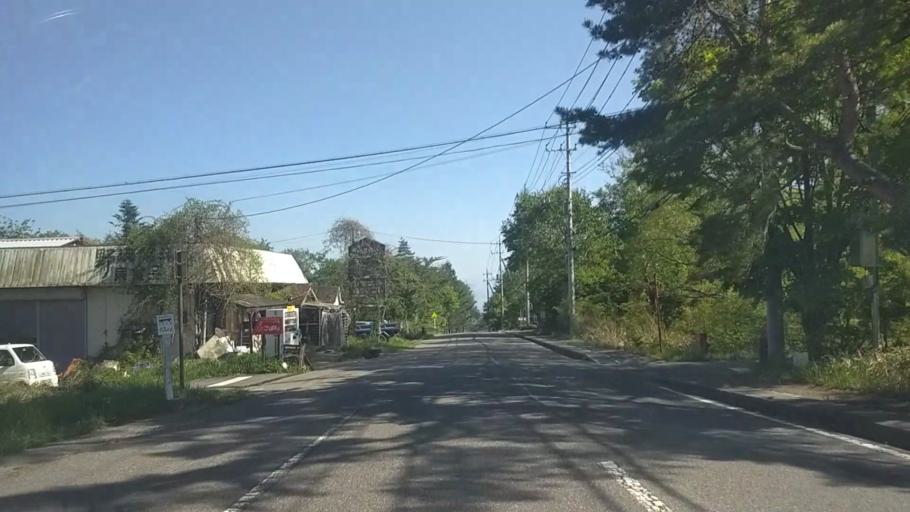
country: JP
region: Yamanashi
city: Nirasaki
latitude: 35.9023
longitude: 138.4093
